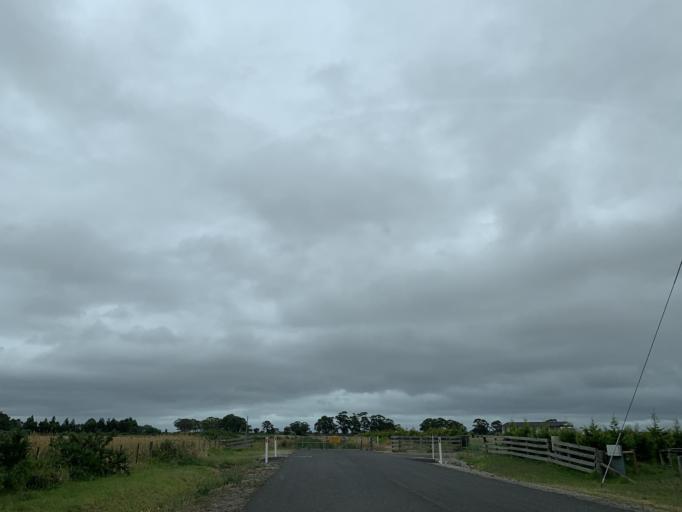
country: AU
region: Victoria
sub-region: Greater Dandenong
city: Keysborough
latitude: -38.0257
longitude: 145.1678
